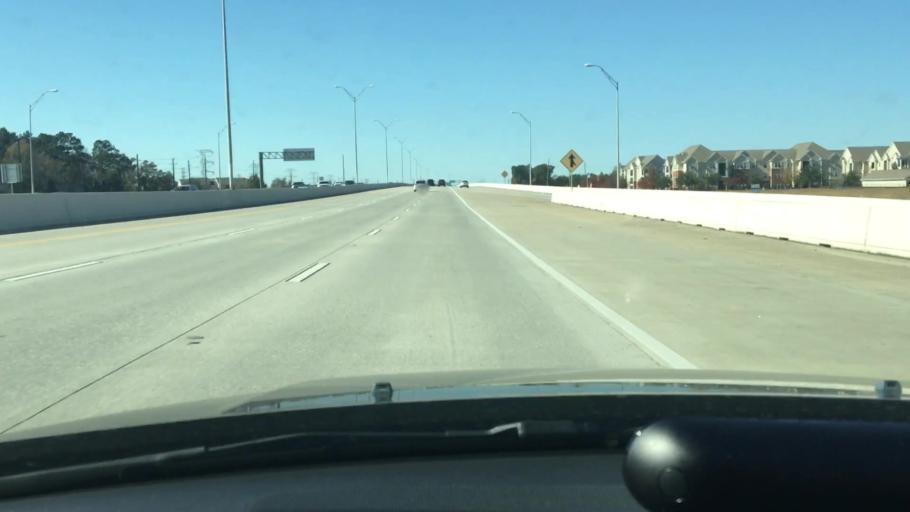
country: US
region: Texas
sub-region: Harris County
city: Humble
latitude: 29.9342
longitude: -95.2298
